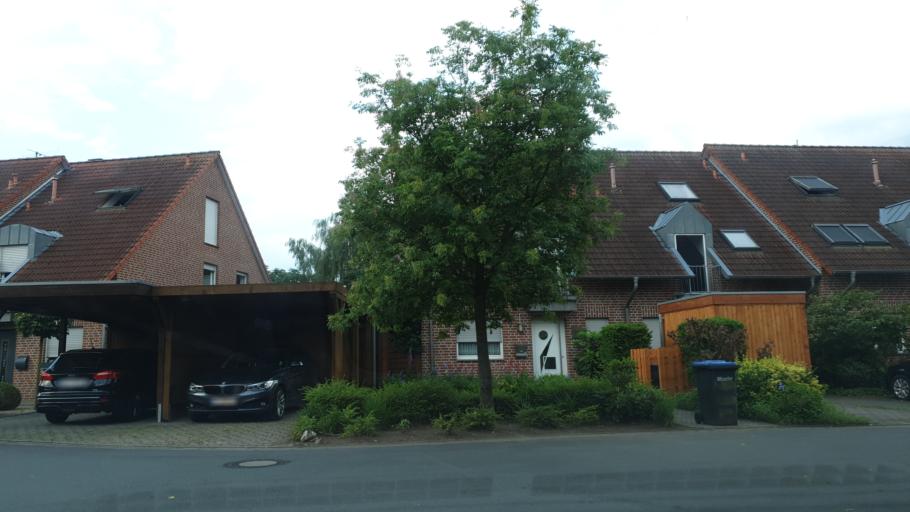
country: DE
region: North Rhine-Westphalia
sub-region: Regierungsbezirk Munster
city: Ostbevern
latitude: 52.0361
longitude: 7.8313
